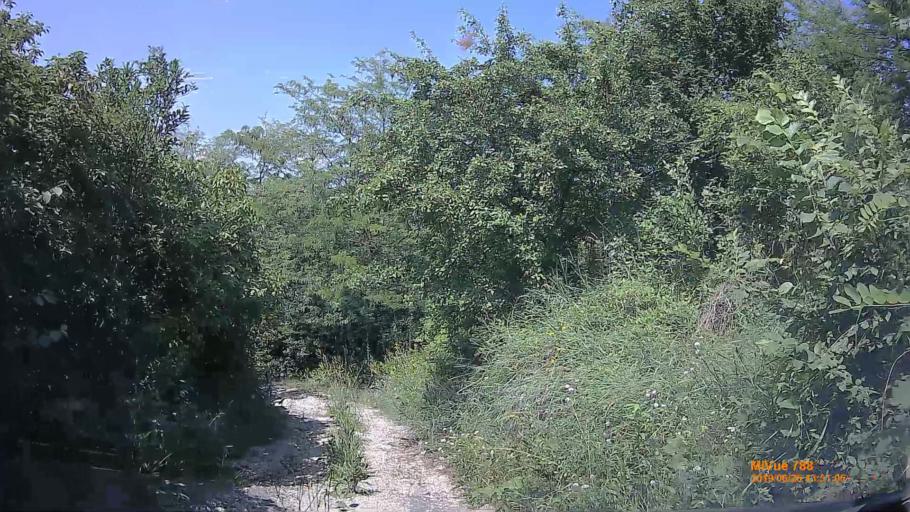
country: HU
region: Komarom-Esztergom
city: Esztergom
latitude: 47.7861
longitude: 18.7532
